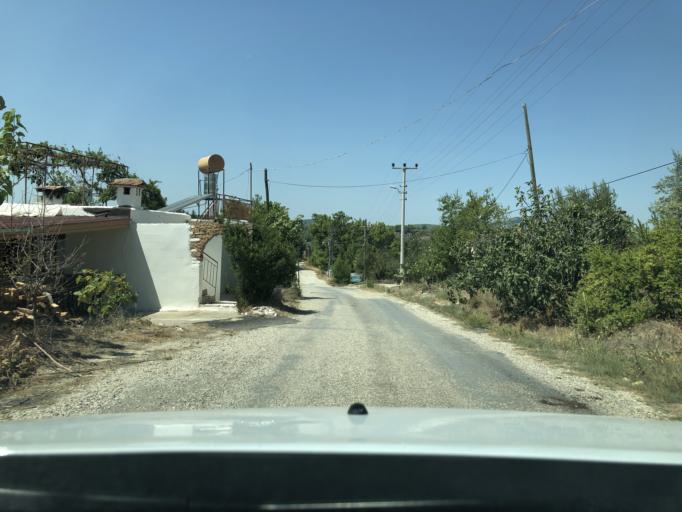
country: TR
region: Antalya
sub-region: Manavgat
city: Kizilagac
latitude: 36.8580
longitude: 31.5554
